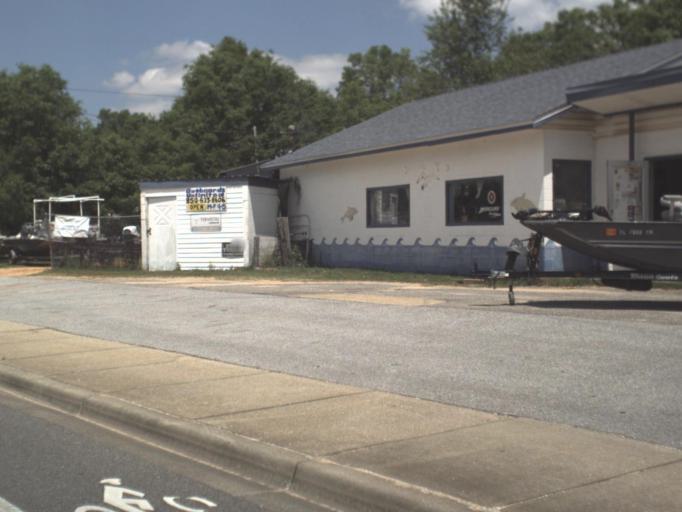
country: US
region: Florida
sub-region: Santa Rosa County
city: Milton
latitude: 30.6553
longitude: -87.0467
